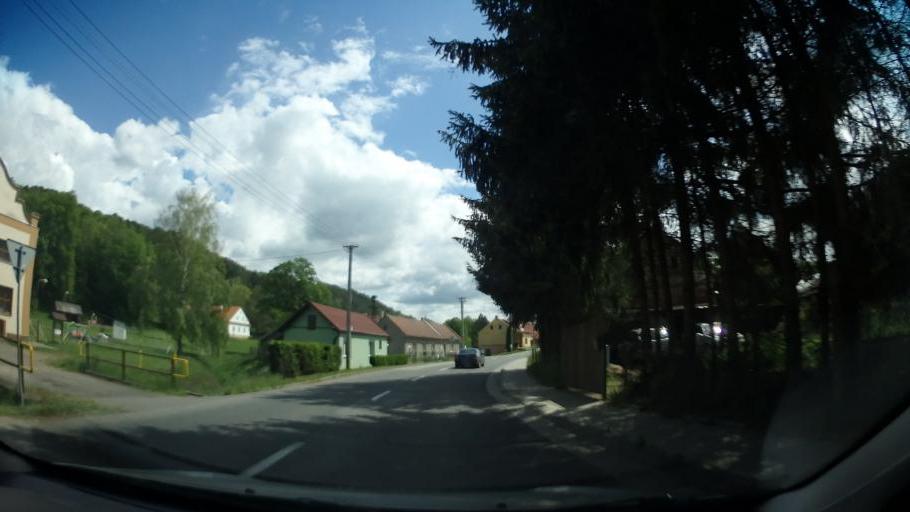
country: CZ
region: Pardubicky
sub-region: Okres Svitavy
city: Moravska Trebova
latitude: 49.7023
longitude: 16.6417
